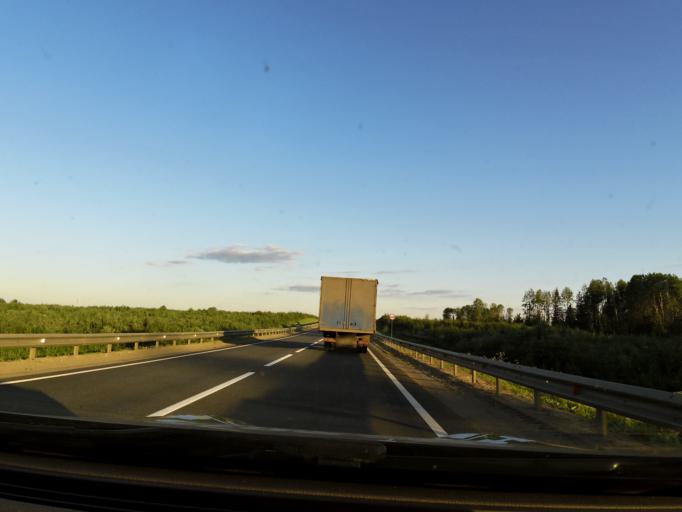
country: RU
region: Jaroslavl
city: Prechistoye
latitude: 58.6423
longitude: 40.3230
